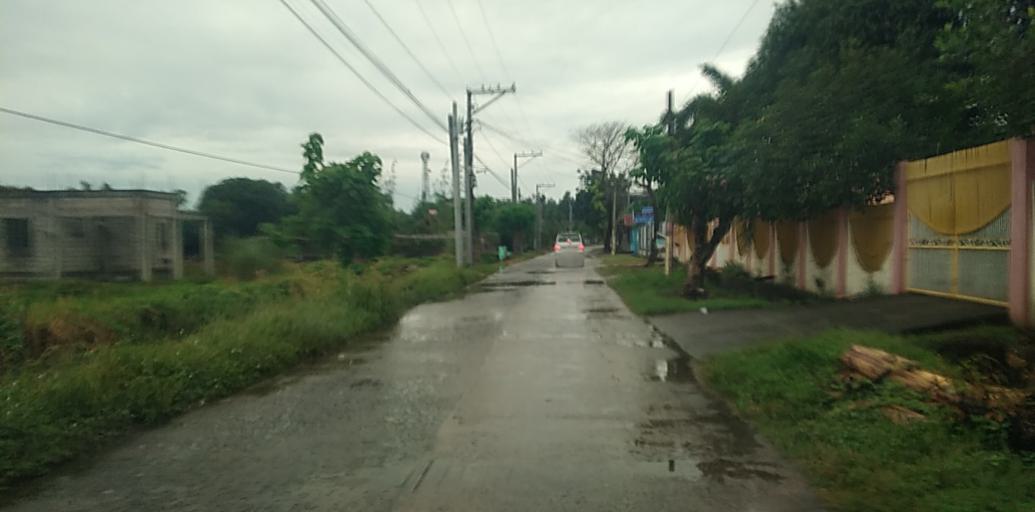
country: PH
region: Central Luzon
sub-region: Province of Pampanga
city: Arayat
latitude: 15.1443
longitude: 120.7404
